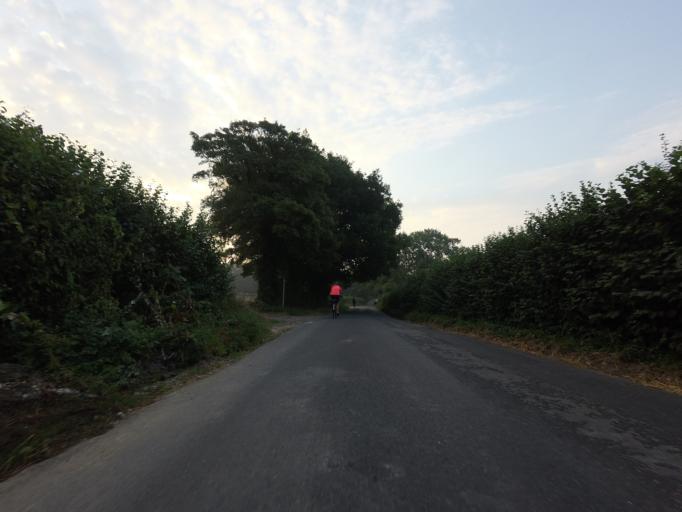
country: GB
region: England
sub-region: Kent
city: Lenham
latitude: 51.1875
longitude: 0.7114
